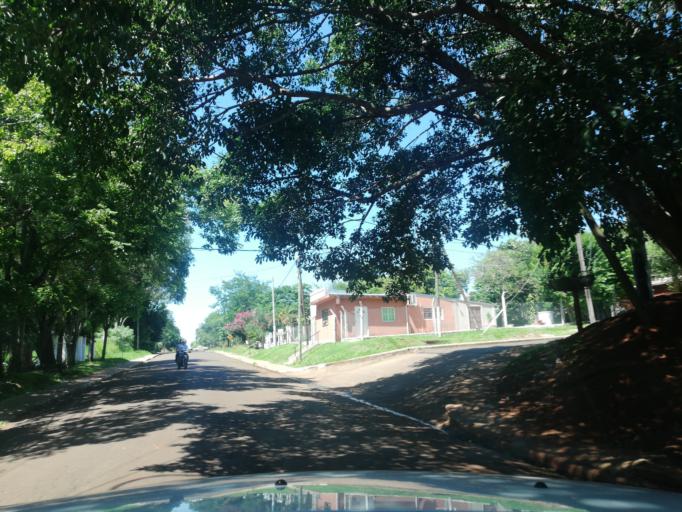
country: AR
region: Misiones
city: Garupa
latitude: -27.4813
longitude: -55.8318
